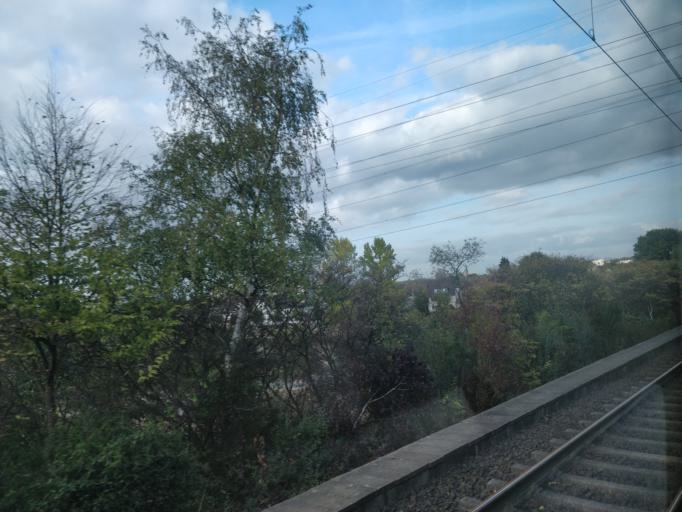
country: DE
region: North Rhine-Westphalia
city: Sankt Augustin
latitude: 50.7891
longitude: 7.1972
